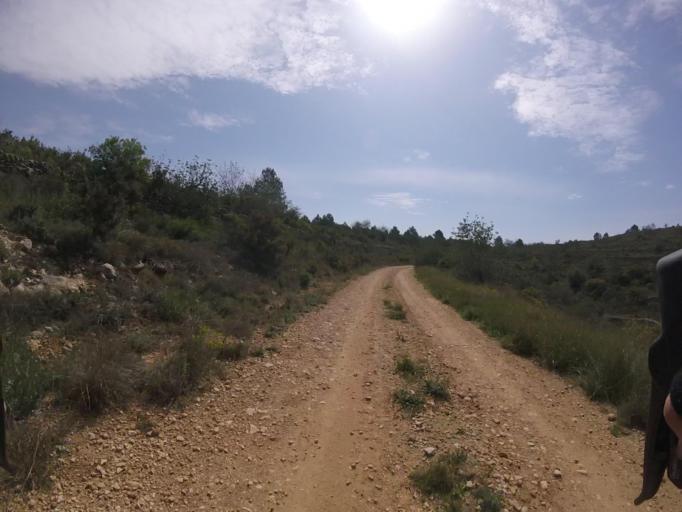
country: ES
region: Valencia
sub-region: Provincia de Castello
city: Cuevas de Vinroma
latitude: 40.2920
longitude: 0.1269
